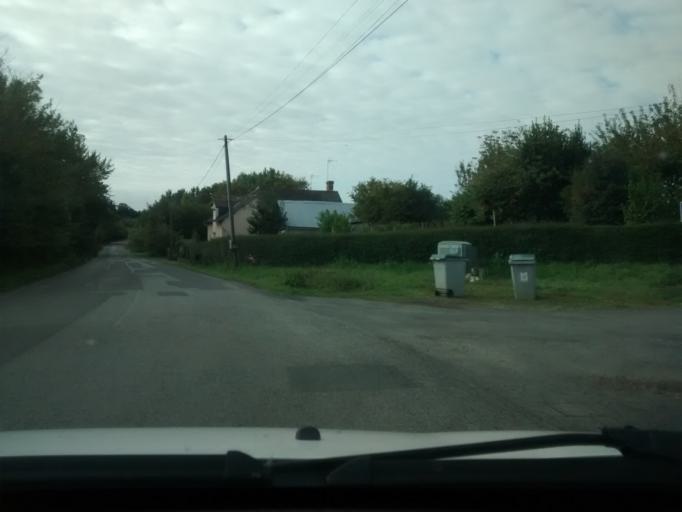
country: FR
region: Brittany
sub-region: Departement d'Ille-et-Vilaine
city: Vezin-le-Coquet
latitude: 48.0888
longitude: -1.7572
